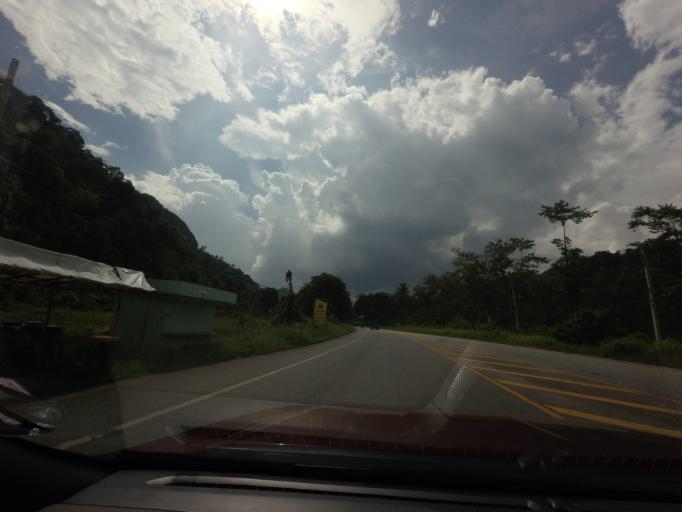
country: TH
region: Yala
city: Than To
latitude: 6.1722
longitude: 101.1786
